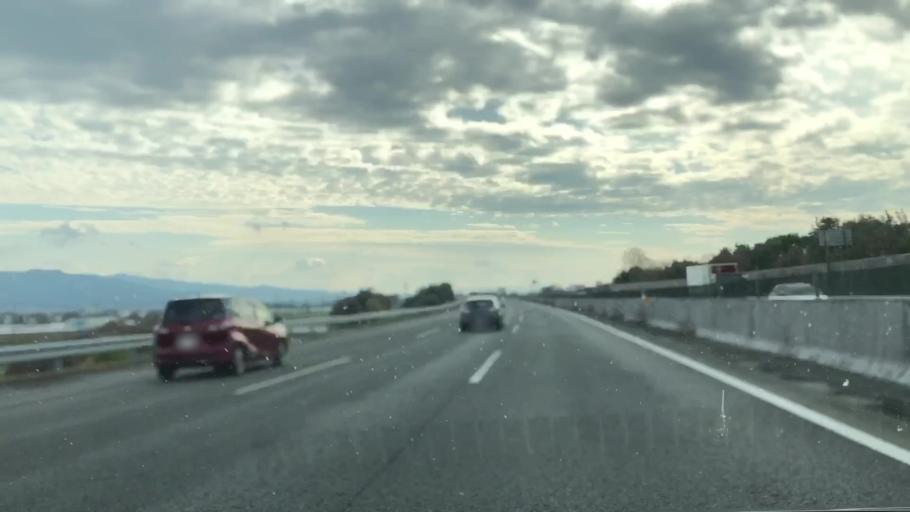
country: JP
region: Saga Prefecture
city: Tosu
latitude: 33.3514
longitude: 130.5377
